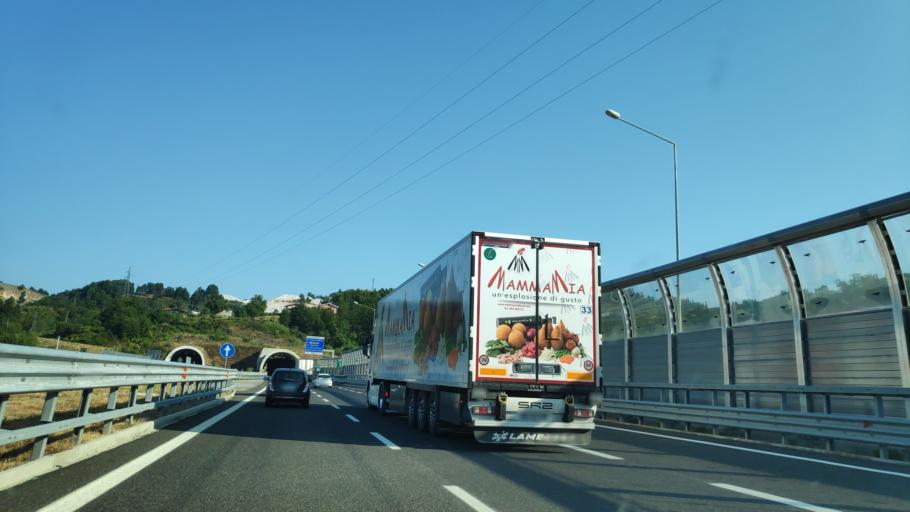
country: IT
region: Basilicate
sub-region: Provincia di Potenza
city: Lagonegro
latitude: 40.1375
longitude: 15.7593
